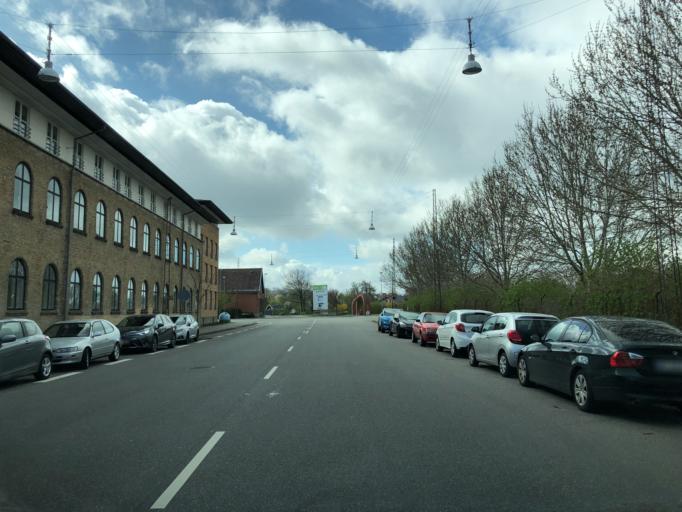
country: DK
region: North Denmark
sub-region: Alborg Kommune
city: Aalborg
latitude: 57.0525
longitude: 9.8916
